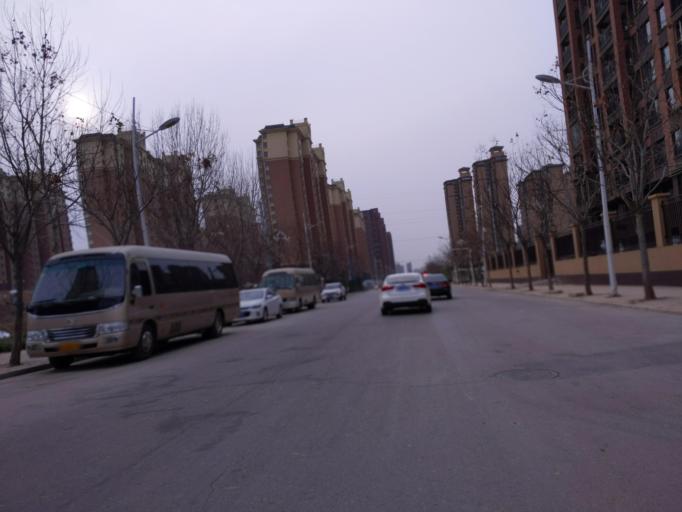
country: CN
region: Henan Sheng
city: Zhongyuanlu
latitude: 35.7425
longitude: 115.0754
